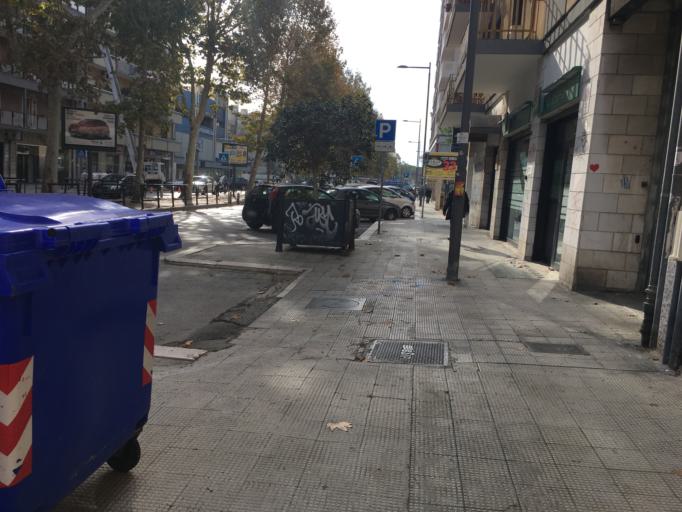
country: IT
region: Apulia
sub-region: Provincia di Bari
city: Bari
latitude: 41.1098
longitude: 16.8738
